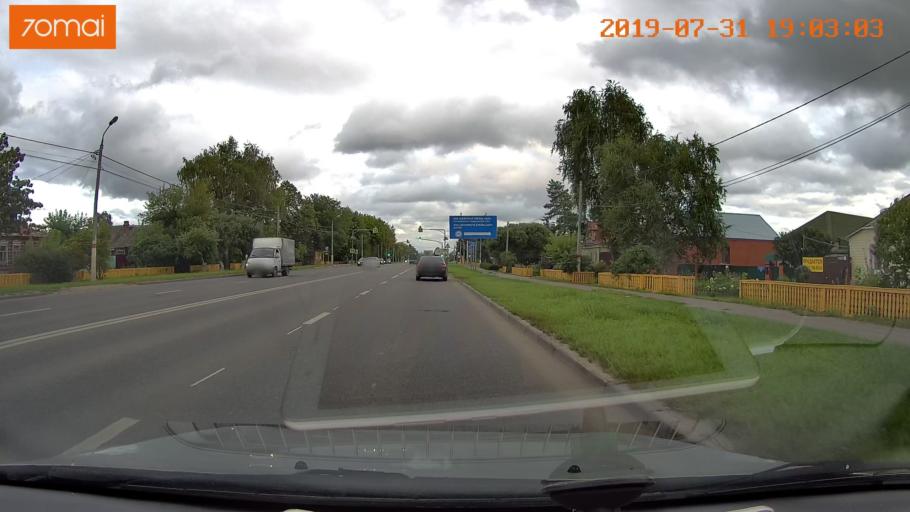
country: RU
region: Moskovskaya
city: Raduzhnyy
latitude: 55.1171
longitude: 38.7360
